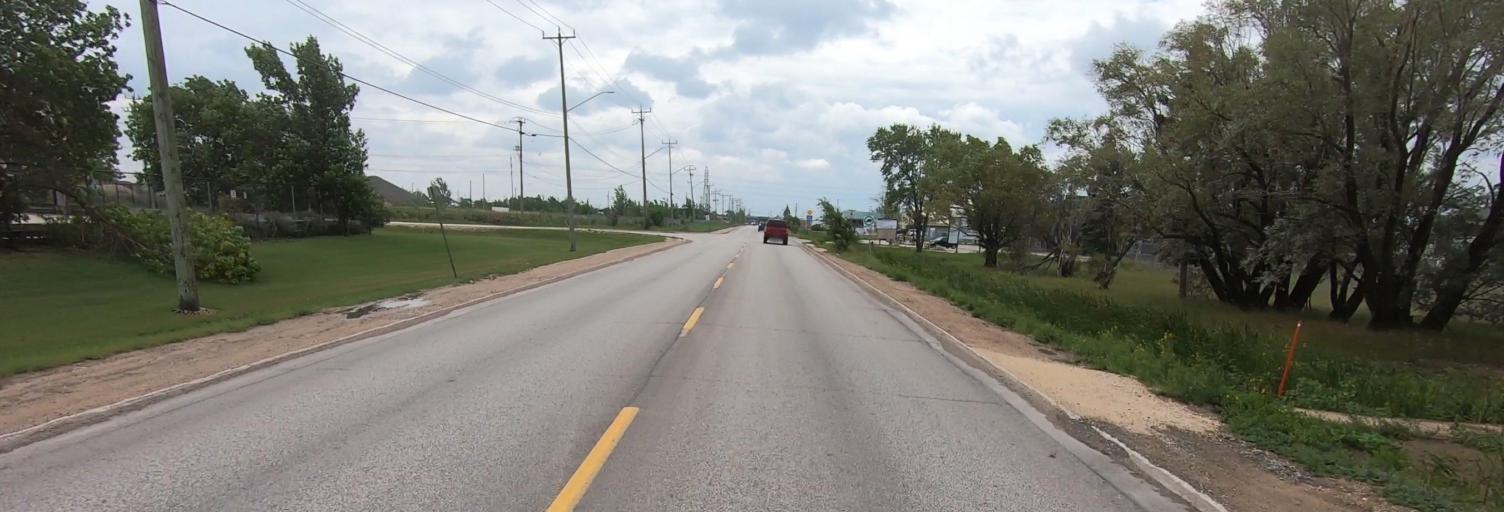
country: CA
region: Manitoba
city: Winnipeg
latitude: 49.8918
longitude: -97.0791
